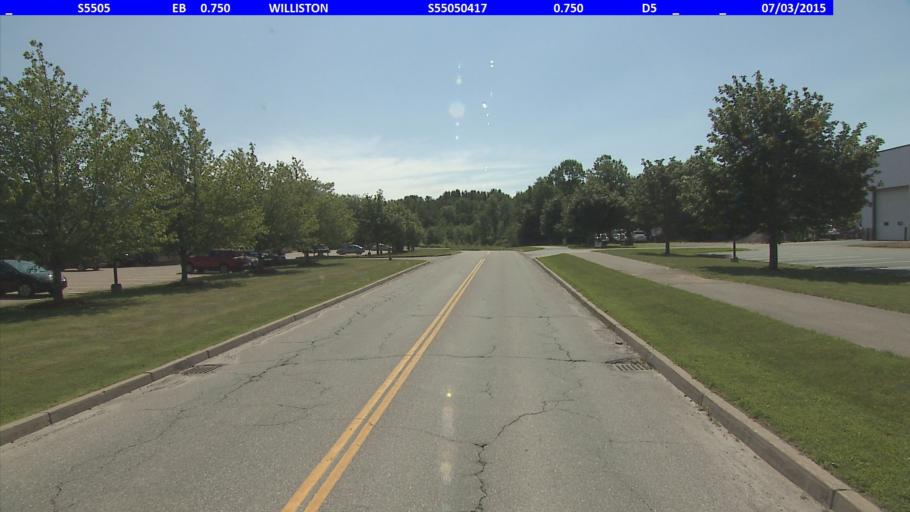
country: US
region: Vermont
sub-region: Chittenden County
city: South Burlington
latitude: 44.4454
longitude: -73.1281
